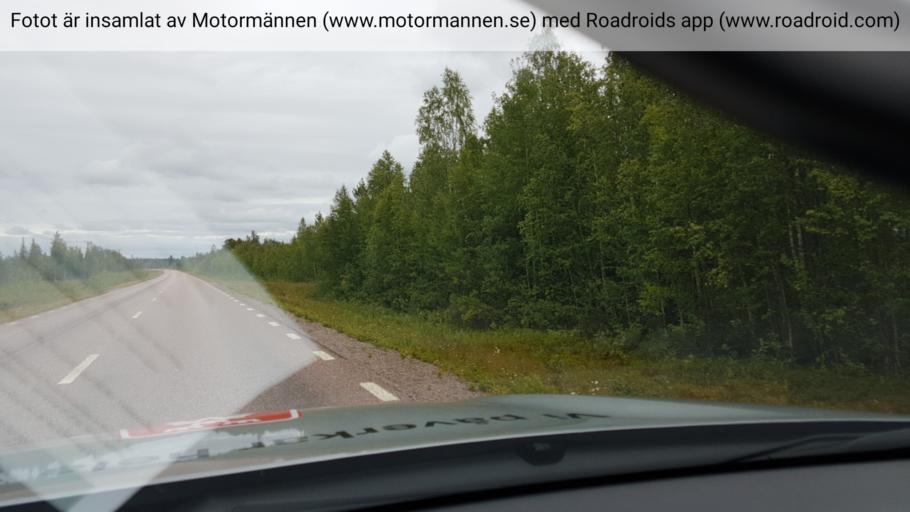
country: SE
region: Norrbotten
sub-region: Pajala Kommun
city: Pajala
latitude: 67.0982
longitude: 22.5818
